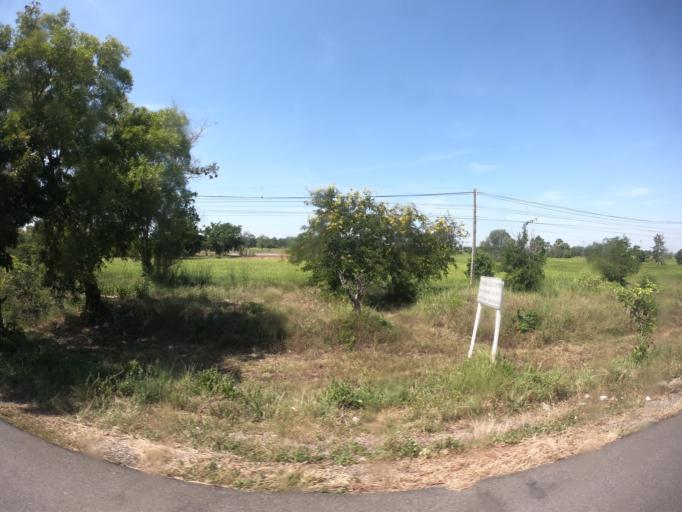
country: TH
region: Nakhon Ratchasima
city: Bua Lai
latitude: 15.7130
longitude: 102.5886
